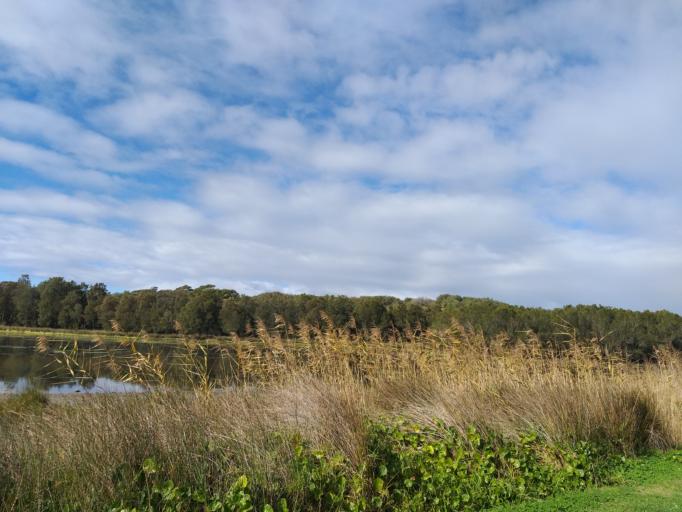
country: AU
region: New South Wales
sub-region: Wollongong
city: East Corrimal
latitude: -34.3728
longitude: 150.9198
